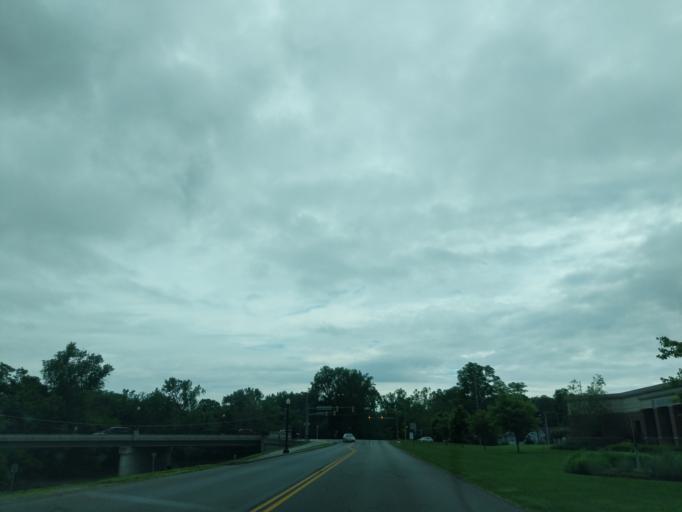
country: US
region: Indiana
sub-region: Delaware County
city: Muncie
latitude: 40.1939
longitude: -85.3988
